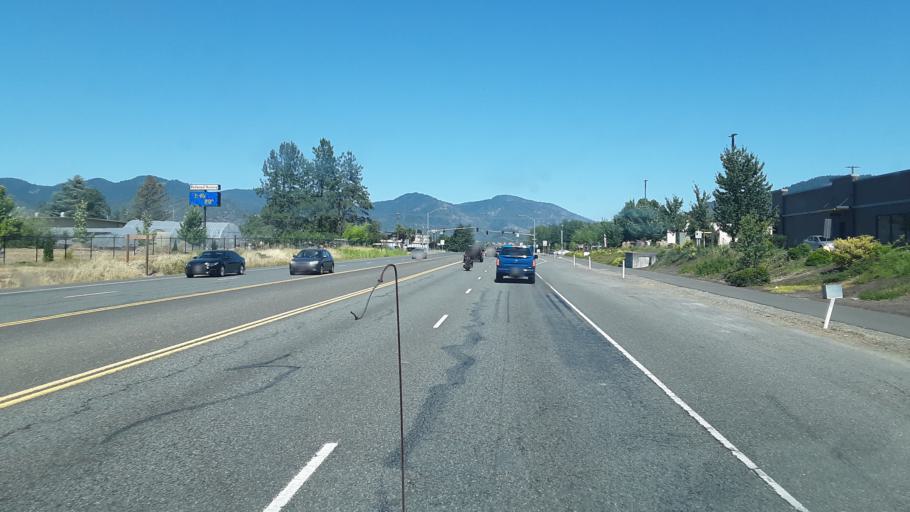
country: US
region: Oregon
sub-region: Josephine County
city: Grants Pass
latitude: 42.4208
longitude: -123.3544
